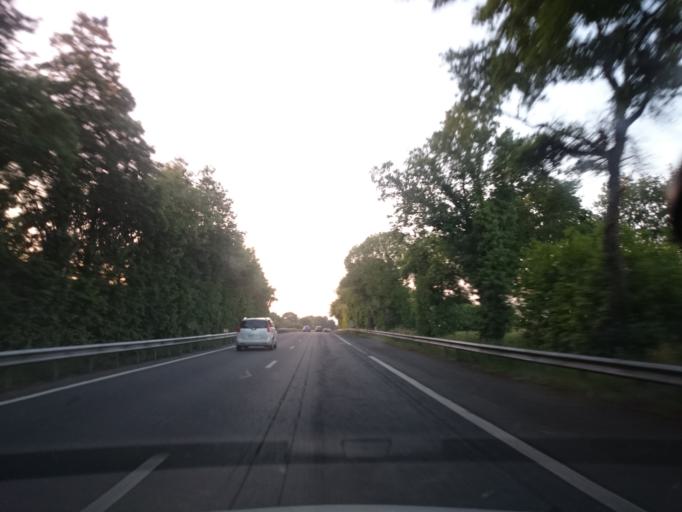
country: FR
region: Brittany
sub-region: Departement d'Ille-et-Vilaine
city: Grand-Fougeray
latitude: 47.7262
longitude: -1.7115
